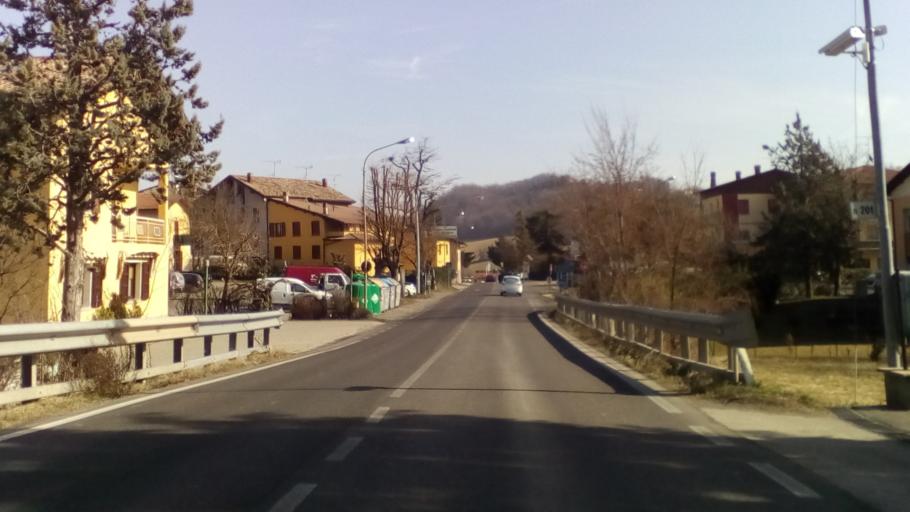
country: IT
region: Emilia-Romagna
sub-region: Provincia di Modena
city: Pavullo nel Frignano
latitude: 44.3120
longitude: 10.8268
